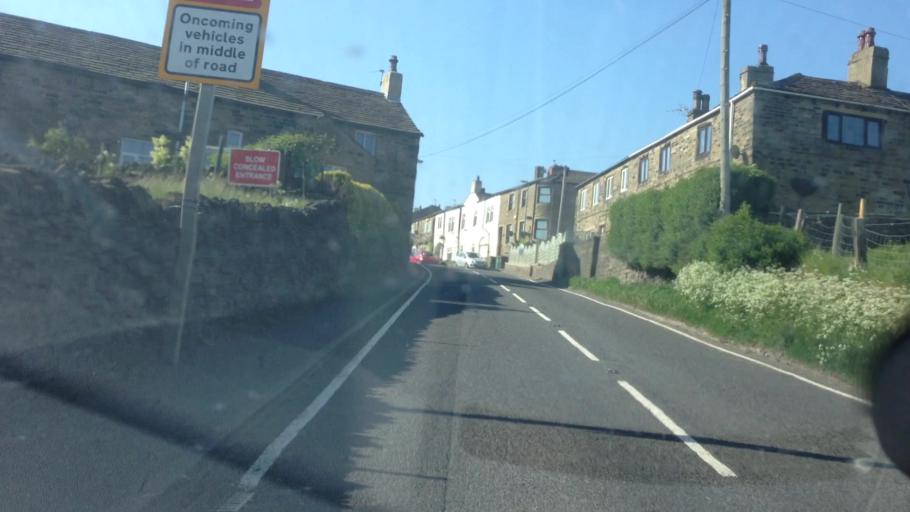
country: GB
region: England
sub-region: Kirklees
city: Mirfield
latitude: 53.6688
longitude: -1.7327
